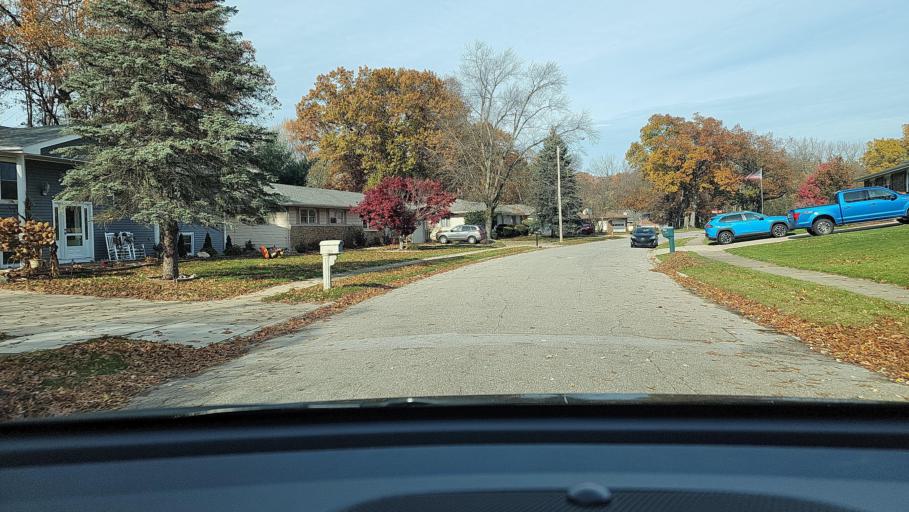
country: US
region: Indiana
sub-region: Porter County
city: Portage
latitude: 41.5777
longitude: -87.2068
